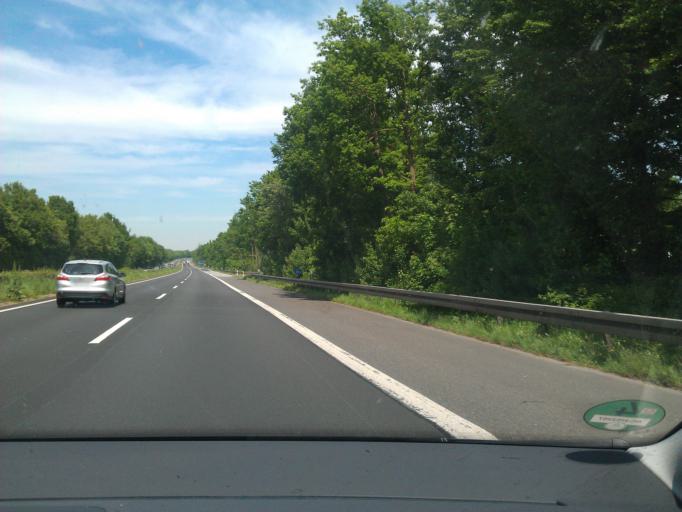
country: DE
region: North Rhine-Westphalia
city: Julich
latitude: 50.9311
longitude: 6.3394
